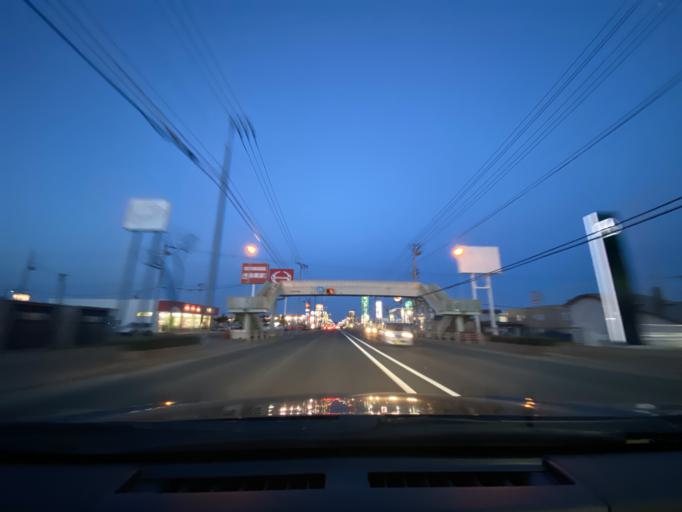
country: JP
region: Hokkaido
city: Kitami
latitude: 43.7974
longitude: 143.8477
